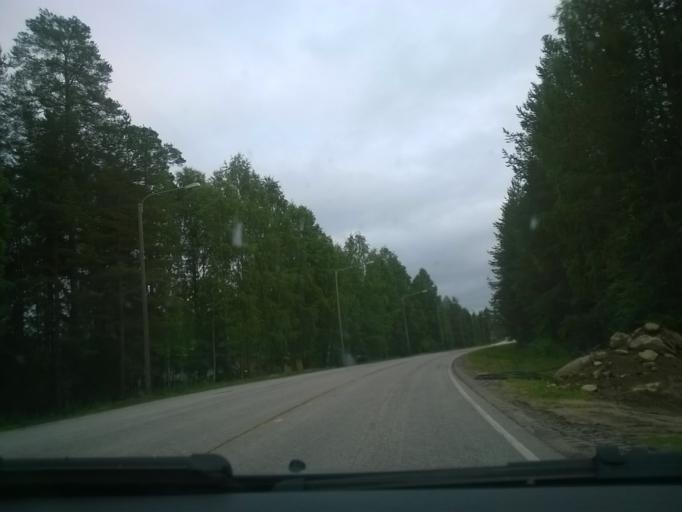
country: FI
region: Kainuu
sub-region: Kehys-Kainuu
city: Kuhmo
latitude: 64.1367
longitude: 29.4560
